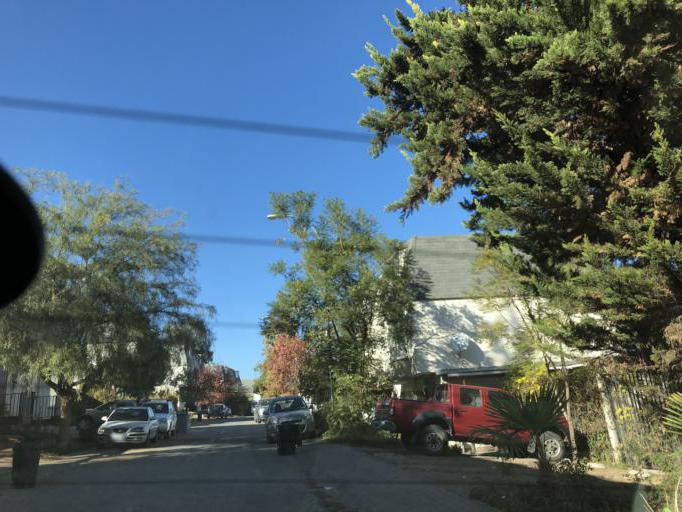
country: CL
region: Santiago Metropolitan
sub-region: Provincia de Cordillera
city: Puente Alto
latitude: -33.5557
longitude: -70.5331
